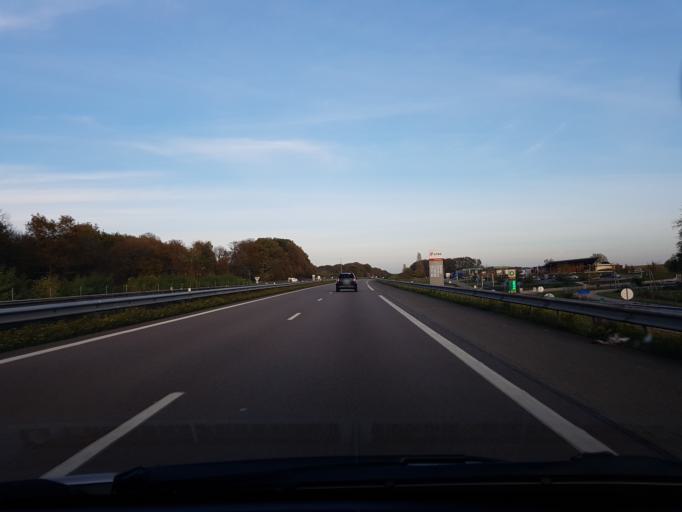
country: FR
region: Franche-Comte
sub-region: Departement du Jura
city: Orchamps
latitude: 47.1474
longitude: 5.5771
